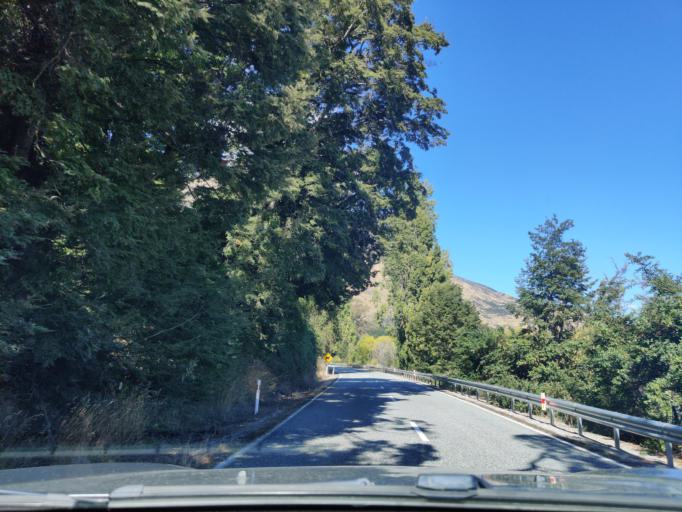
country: NZ
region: Otago
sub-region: Queenstown-Lakes District
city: Queenstown
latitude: -44.9983
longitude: 168.4366
